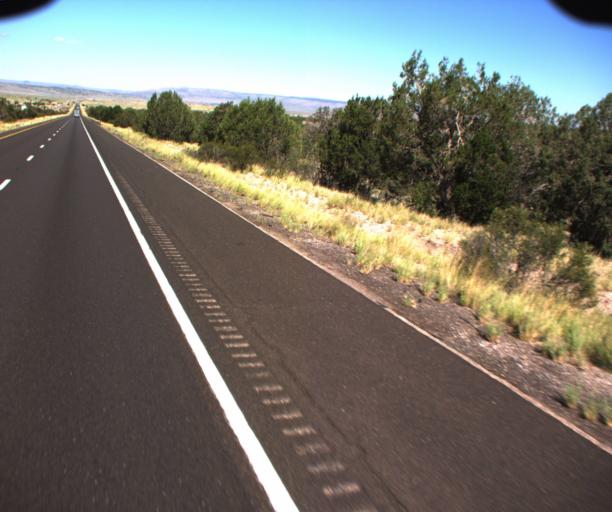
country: US
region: Arizona
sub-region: Yavapai County
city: Paulden
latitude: 35.2809
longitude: -112.7861
